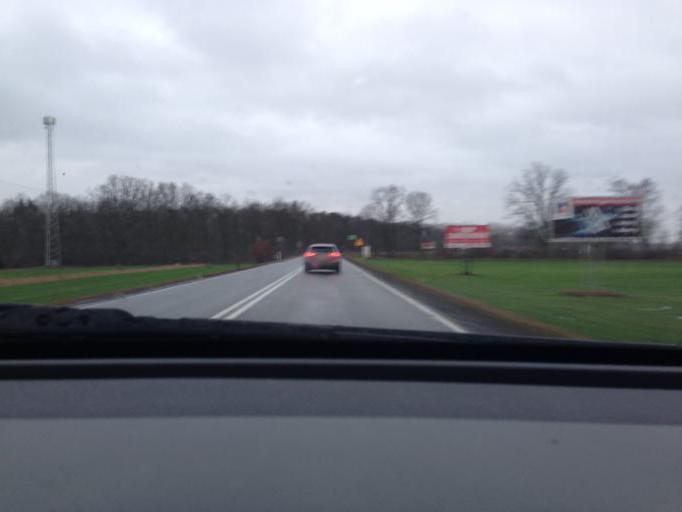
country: PL
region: Opole Voivodeship
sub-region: Powiat opolski
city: Wegry
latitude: 50.7085
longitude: 17.9857
